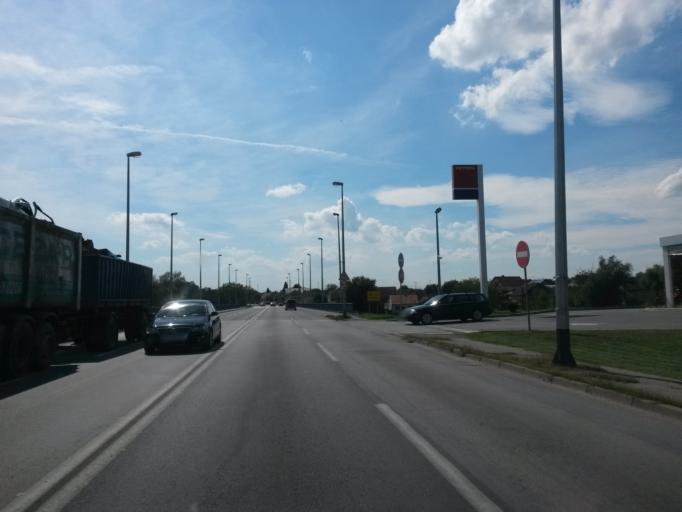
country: HR
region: Vukovarsko-Srijemska
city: Vinkovci
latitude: 45.2809
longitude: 18.8087
